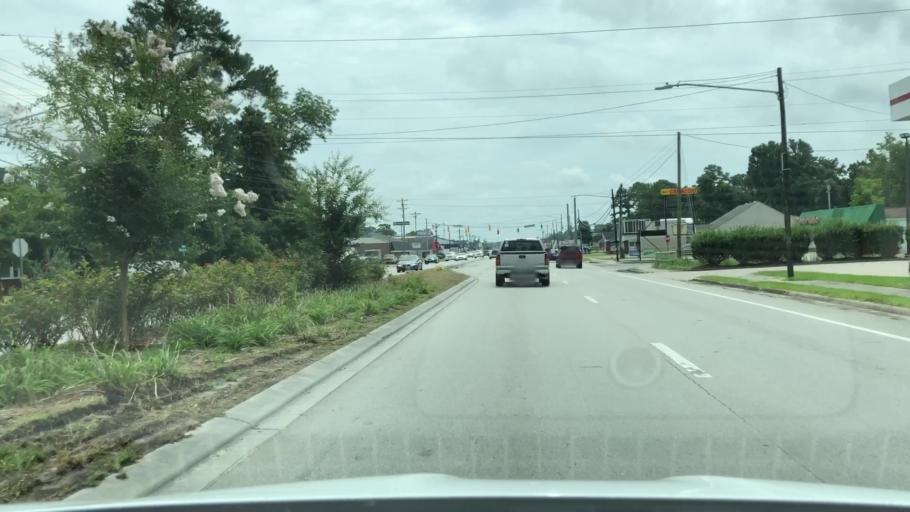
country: US
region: North Carolina
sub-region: Craven County
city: Havelock
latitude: 34.8722
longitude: -76.9021
